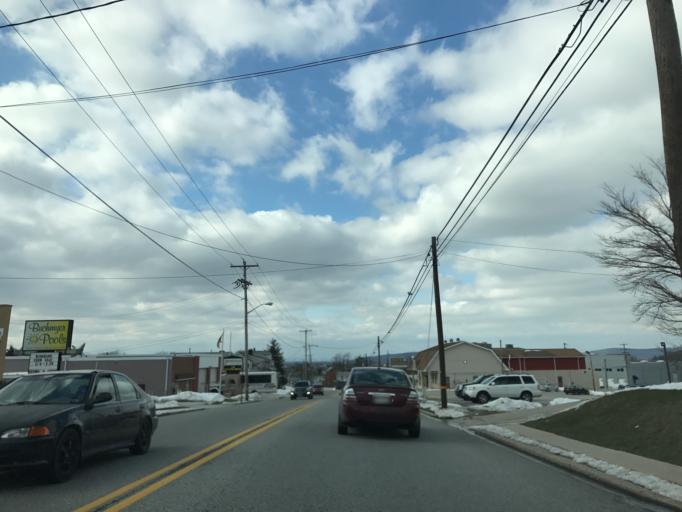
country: US
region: Pennsylvania
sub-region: York County
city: Parkville
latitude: 39.7823
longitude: -76.9640
